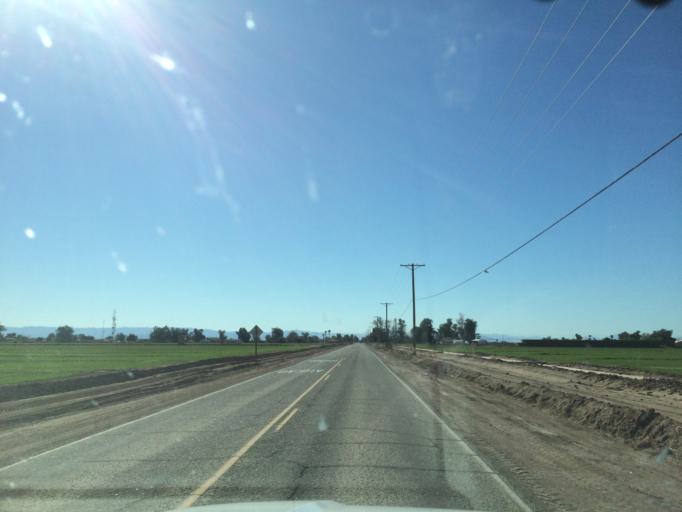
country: US
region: California
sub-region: Imperial County
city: Heber
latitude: 32.7524
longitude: -115.5530
